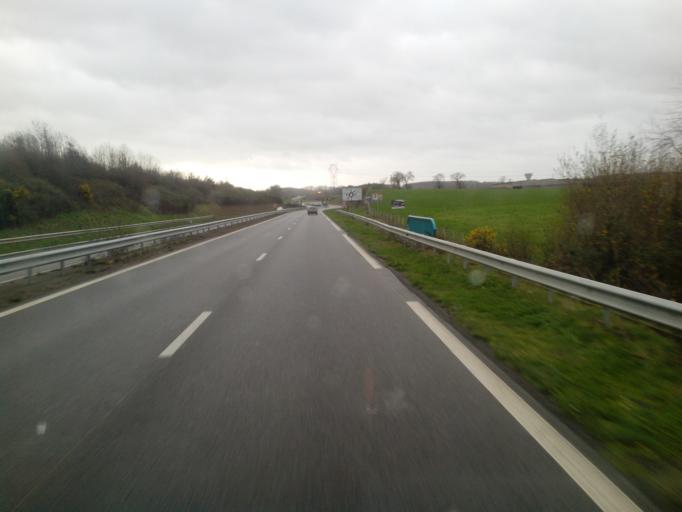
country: FR
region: Brittany
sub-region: Departement d'Ille-et-Vilaine
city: Betton
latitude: 48.1591
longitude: -1.6257
